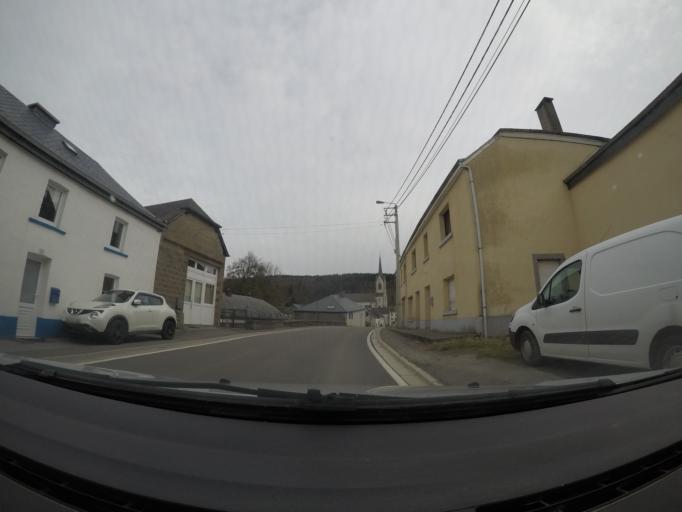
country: BE
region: Wallonia
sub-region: Province du Luxembourg
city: Martelange
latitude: 49.8437
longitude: 5.7213
